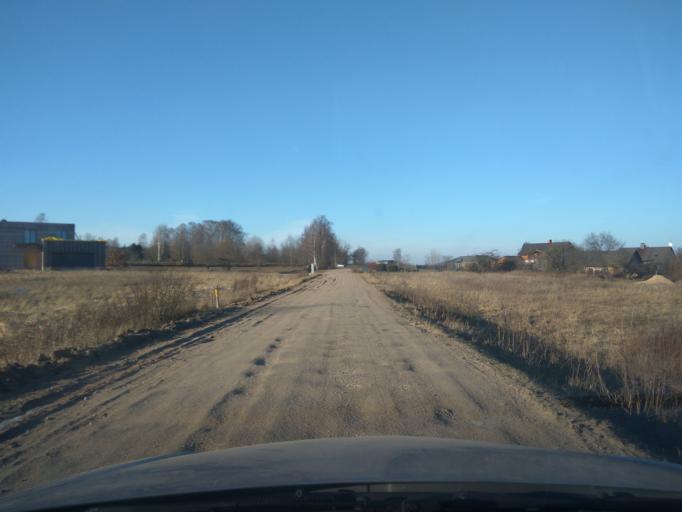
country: LV
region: Kuldigas Rajons
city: Kuldiga
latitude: 56.9694
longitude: 21.9401
